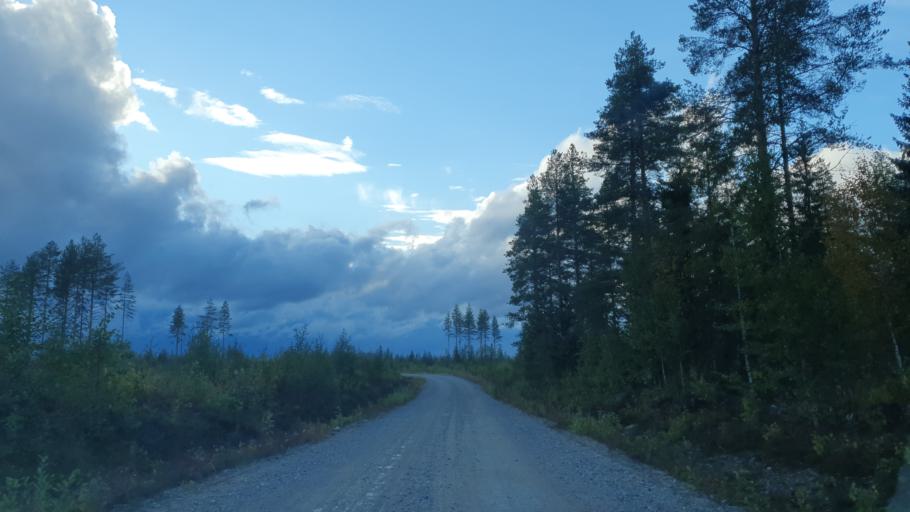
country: FI
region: Kainuu
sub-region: Kehys-Kainuu
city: Kuhmo
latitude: 64.3355
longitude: 29.9314
